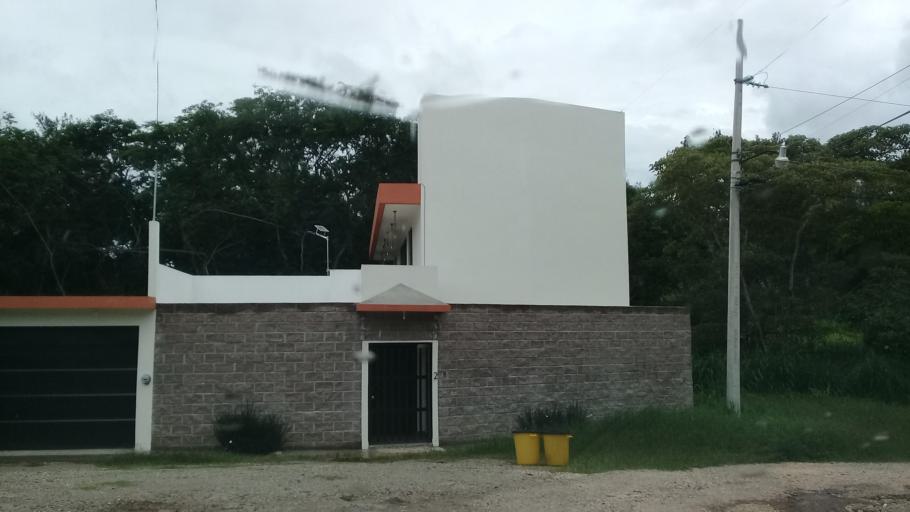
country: MX
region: Veracruz
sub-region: Emiliano Zapata
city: Jacarandas
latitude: 19.5032
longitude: -96.8402
